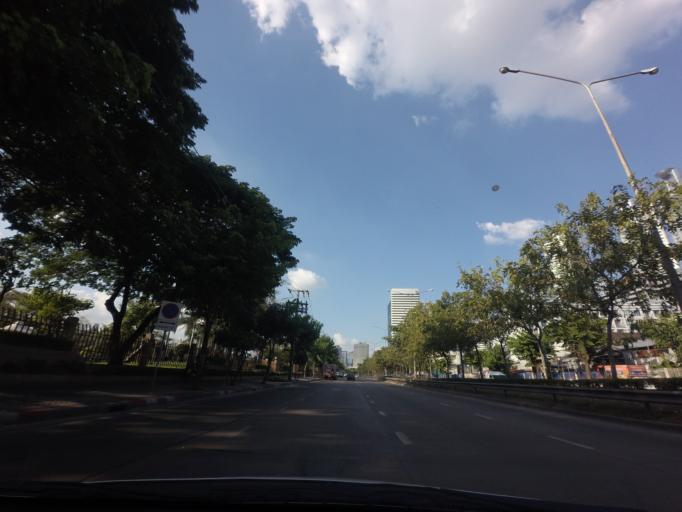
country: TH
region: Bangkok
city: Khlong Toei
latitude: 13.7268
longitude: 100.5602
